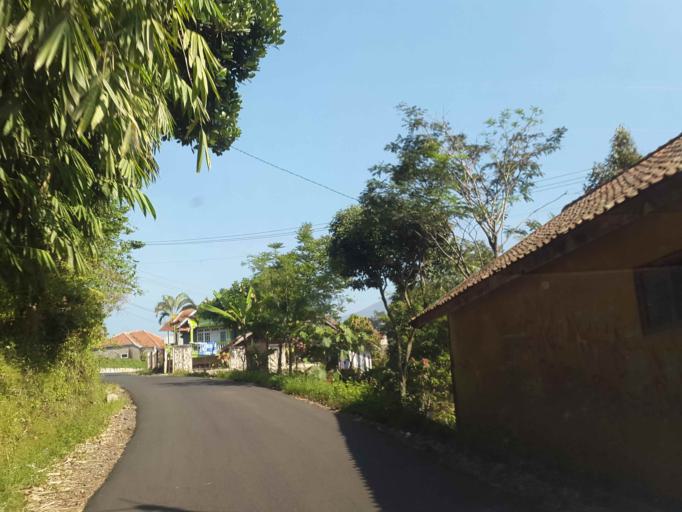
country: ID
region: West Java
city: Cibeber
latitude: -6.8575
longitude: 107.0719
